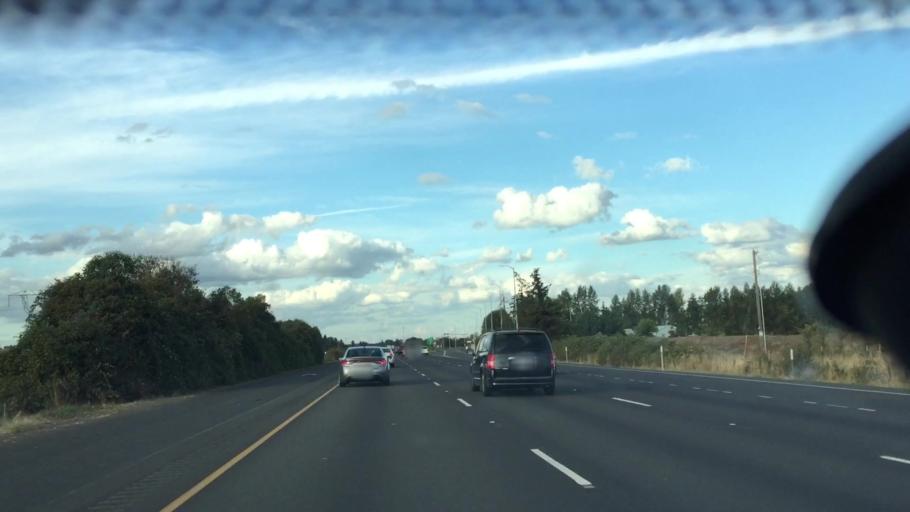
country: US
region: Oregon
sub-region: Marion County
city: Woodburn
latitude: 45.1714
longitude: -122.8597
